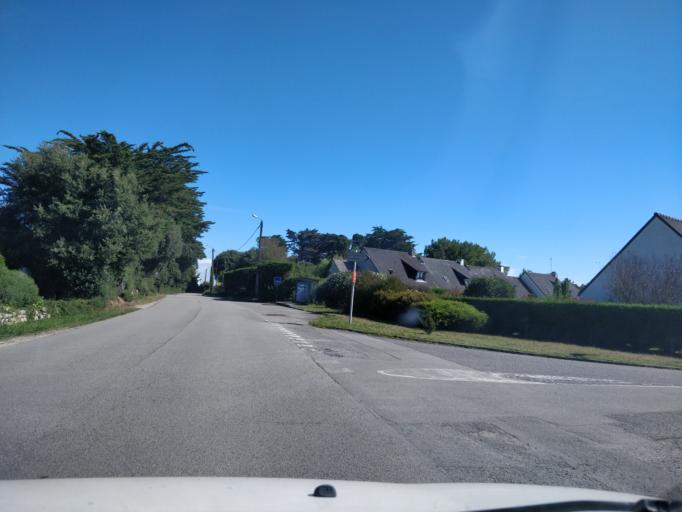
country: FR
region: Brittany
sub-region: Departement du Morbihan
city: Locmariaquer
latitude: 47.5754
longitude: -2.9525
